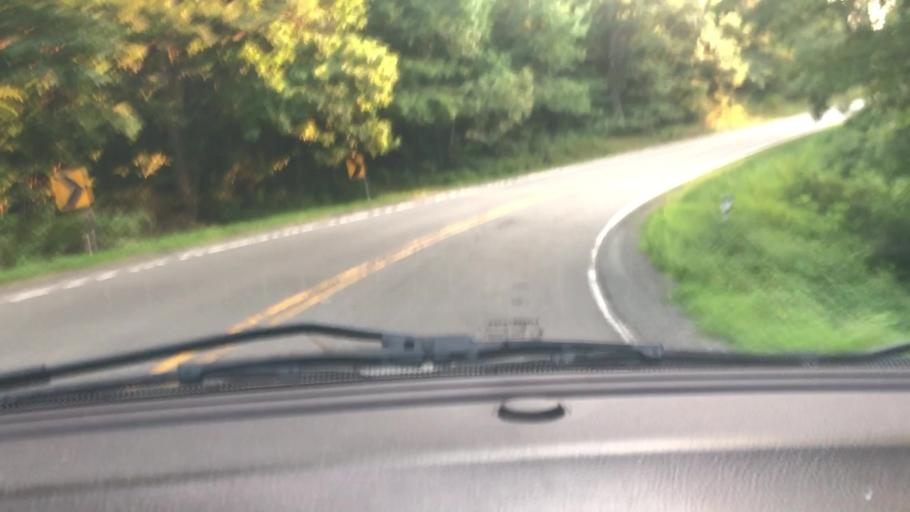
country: US
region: Virginia
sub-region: Patrick County
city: Stuart
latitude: 36.7124
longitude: -80.3385
